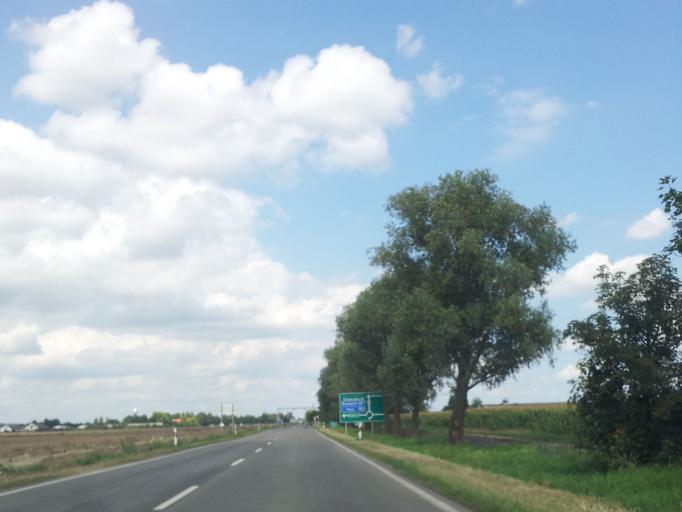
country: HU
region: Baranya
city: Mohacs
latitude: 45.9686
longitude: 18.6729
